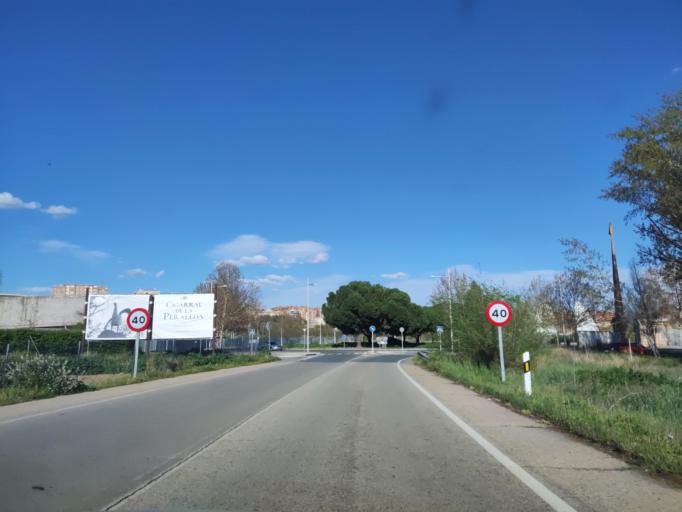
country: ES
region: Castille-La Mancha
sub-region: Province of Toledo
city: Toledo
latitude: 39.8743
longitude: -4.0477
